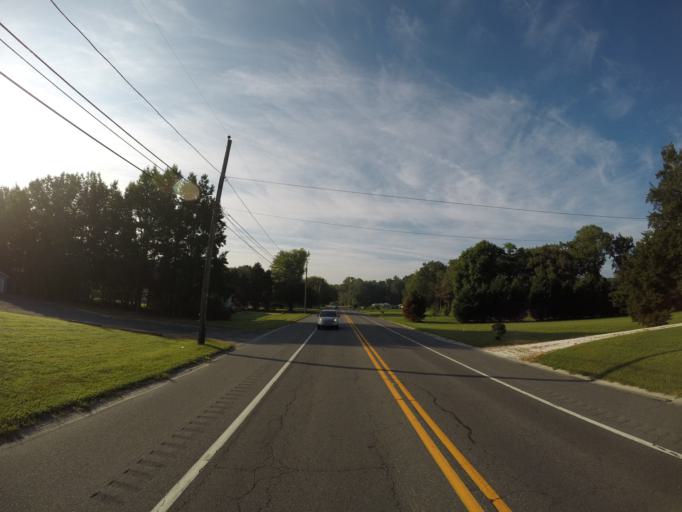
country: US
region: Delaware
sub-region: Sussex County
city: Selbyville
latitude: 38.4866
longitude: -75.1600
